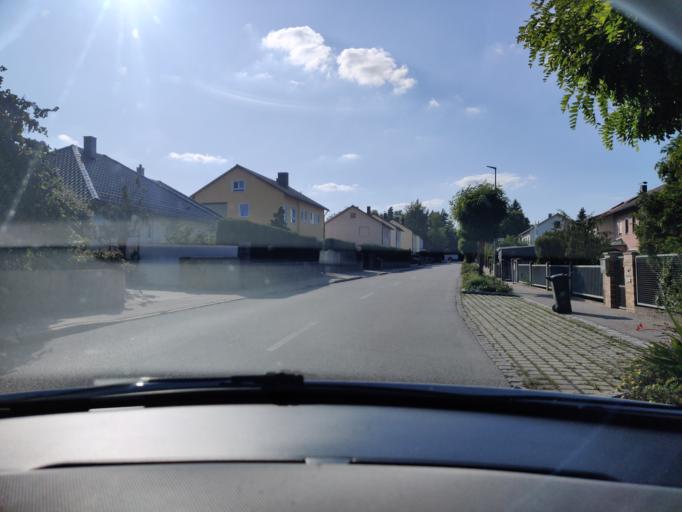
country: DE
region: Bavaria
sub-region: Upper Palatinate
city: Schwandorf in Bayern
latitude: 49.3266
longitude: 12.1256
